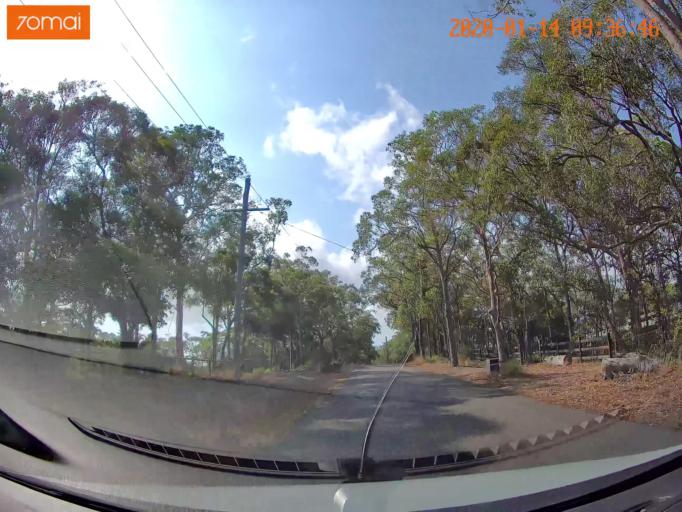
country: AU
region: New South Wales
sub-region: Wyong Shire
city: Kingfisher Shores
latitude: -33.1134
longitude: 151.5576
